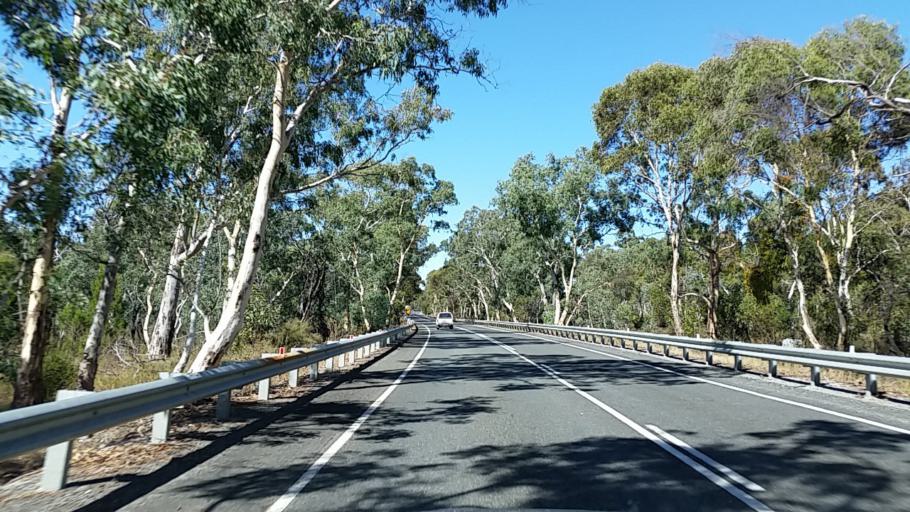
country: AU
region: South Australia
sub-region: Adelaide Hills
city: Birdwood
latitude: -34.7371
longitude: 138.9739
